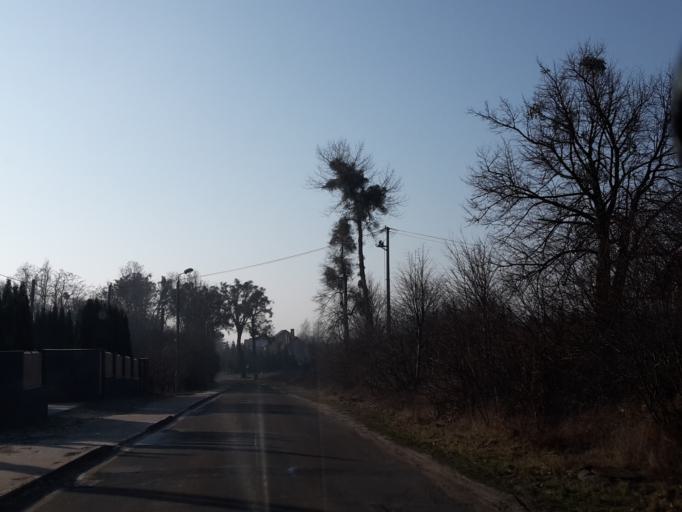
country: PL
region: Kujawsko-Pomorskie
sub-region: Powiat brodnicki
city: Brodnica
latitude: 53.2807
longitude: 19.4110
